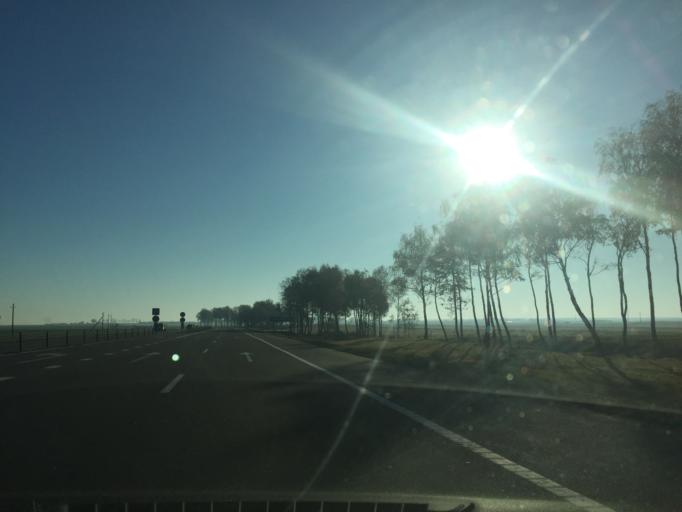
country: BY
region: Minsk
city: Luhavaya Slabada
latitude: 53.7626
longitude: 27.8754
